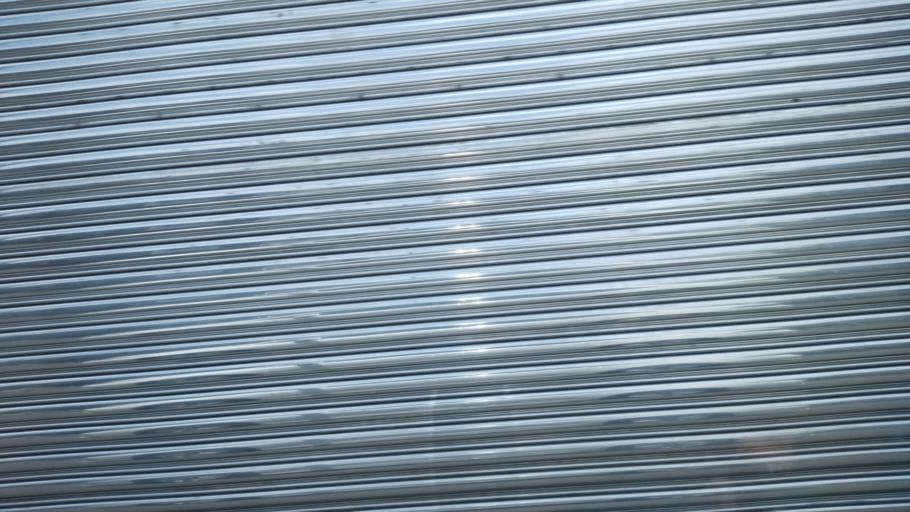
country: TW
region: Taipei
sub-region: Taipei
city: Banqiao
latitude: 24.9480
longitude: 121.4923
